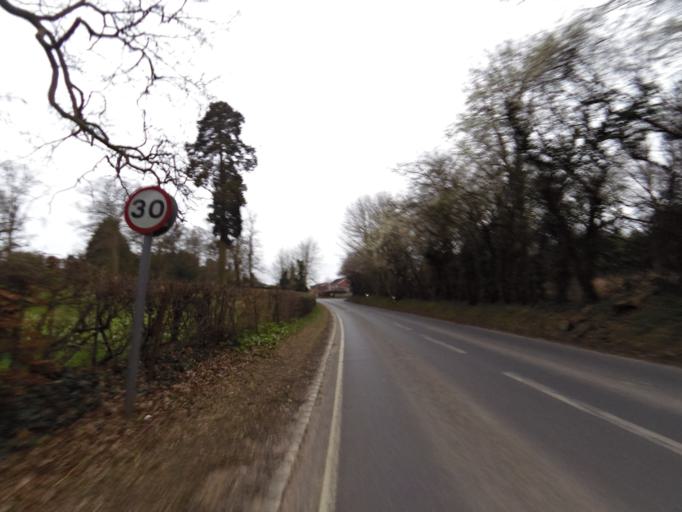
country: GB
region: England
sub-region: Suffolk
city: Ipswich
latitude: 52.0867
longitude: 1.1504
